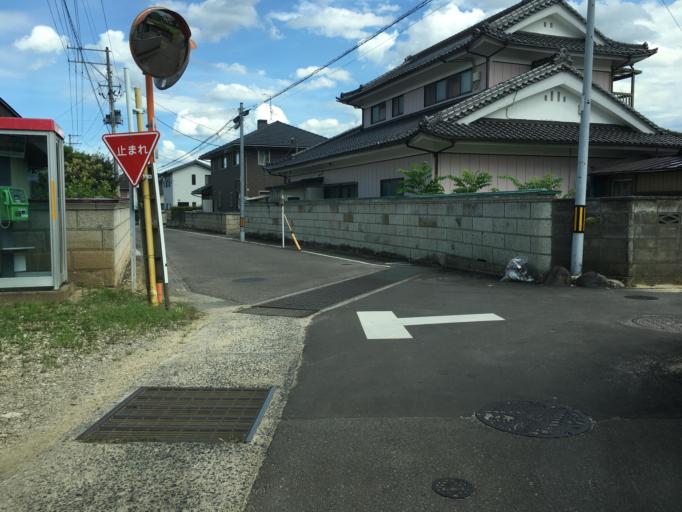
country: JP
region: Fukushima
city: Fukushima-shi
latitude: 37.7761
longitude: 140.4282
